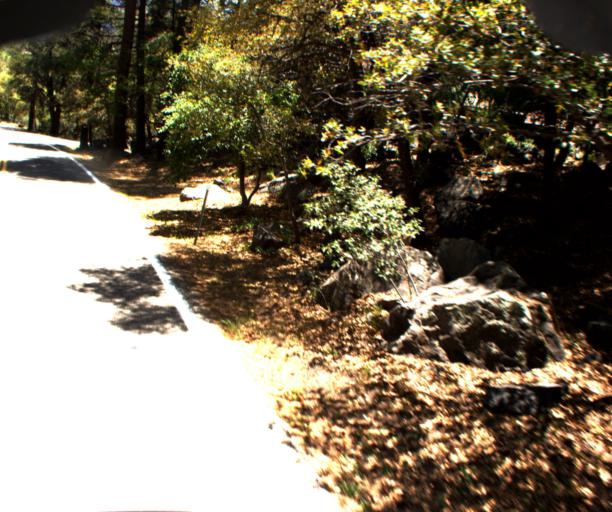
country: US
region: Arizona
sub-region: Coconino County
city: Sedona
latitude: 34.9634
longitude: -111.7531
